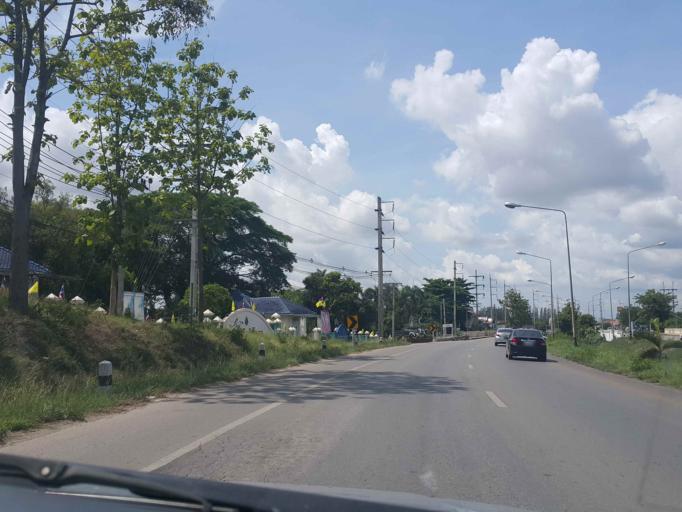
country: TH
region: Phayao
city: Phayao
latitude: 19.1611
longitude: 99.9142
